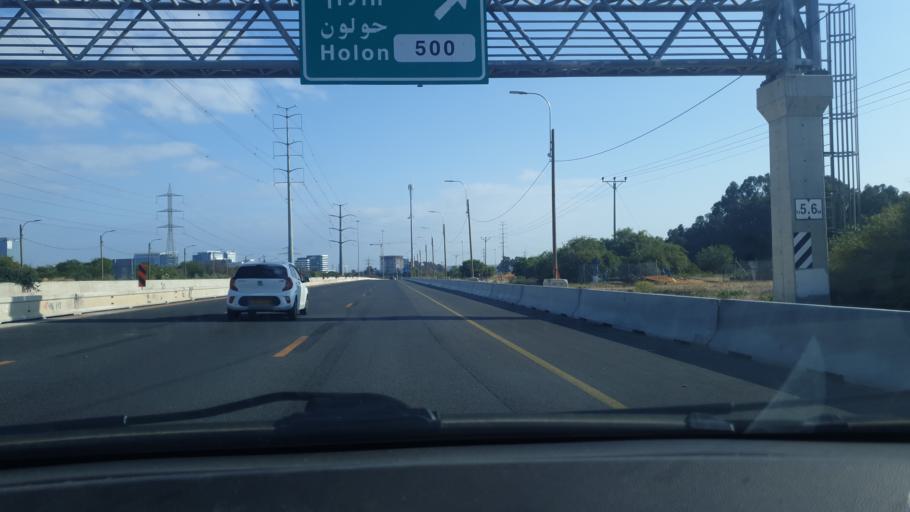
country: IL
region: Central District
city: Rishon LeZiyyon
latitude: 31.9915
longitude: 34.7987
